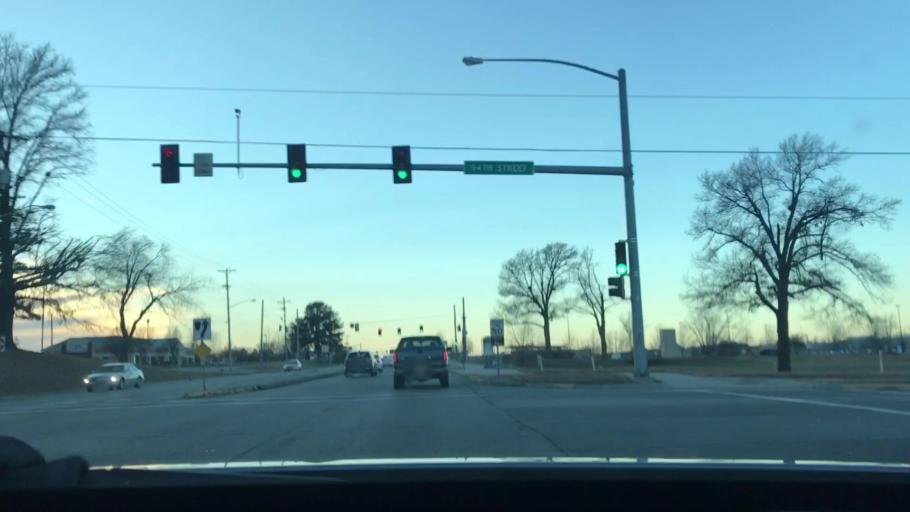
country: US
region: Kansas
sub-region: Wyandotte County
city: Edwardsville
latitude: 39.1165
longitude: -94.7978
